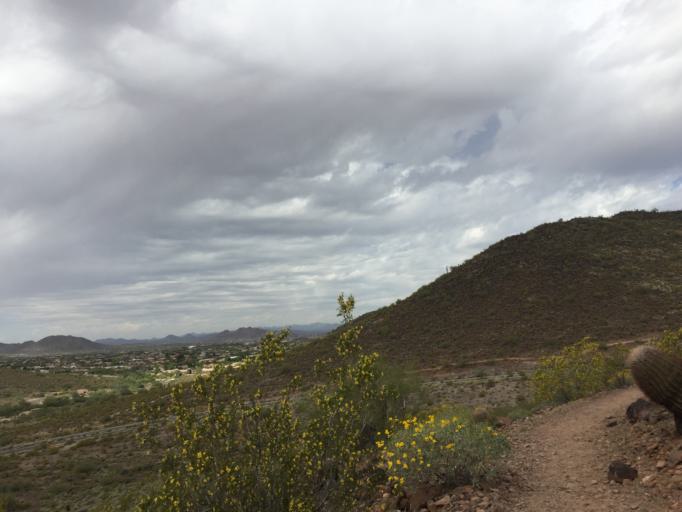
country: US
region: Arizona
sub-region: Maricopa County
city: Peoria
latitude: 33.6898
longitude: -112.1852
